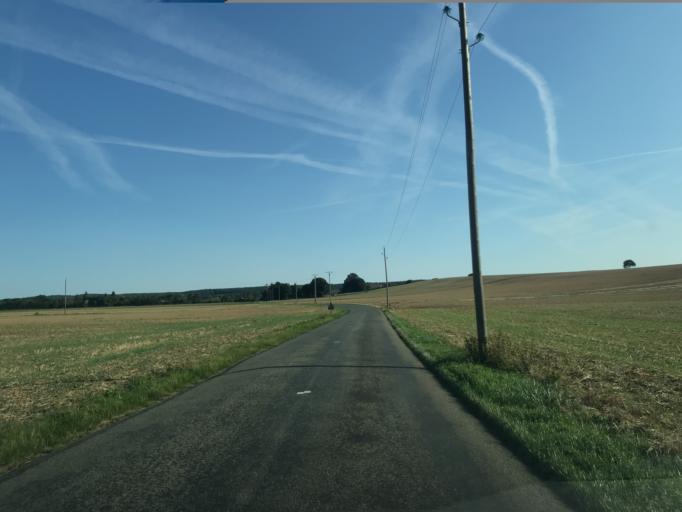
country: FR
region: Haute-Normandie
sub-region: Departement de l'Eure
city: Houlbec-Cocherel
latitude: 49.0600
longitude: 1.2975
